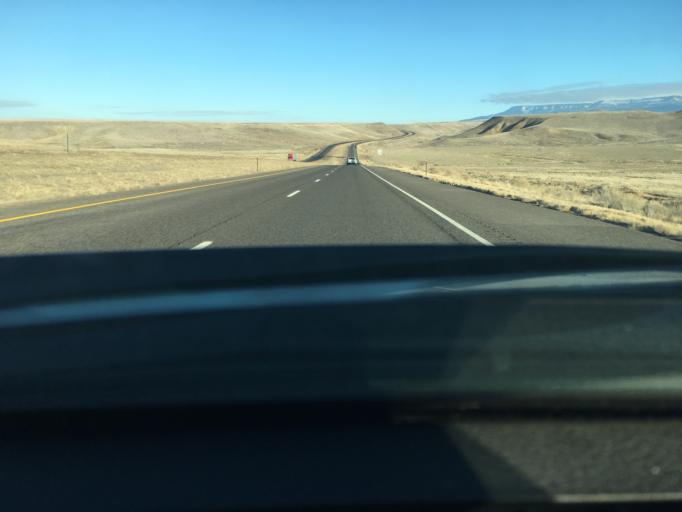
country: US
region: Colorado
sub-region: Delta County
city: Delta
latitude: 38.8229
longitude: -108.2970
